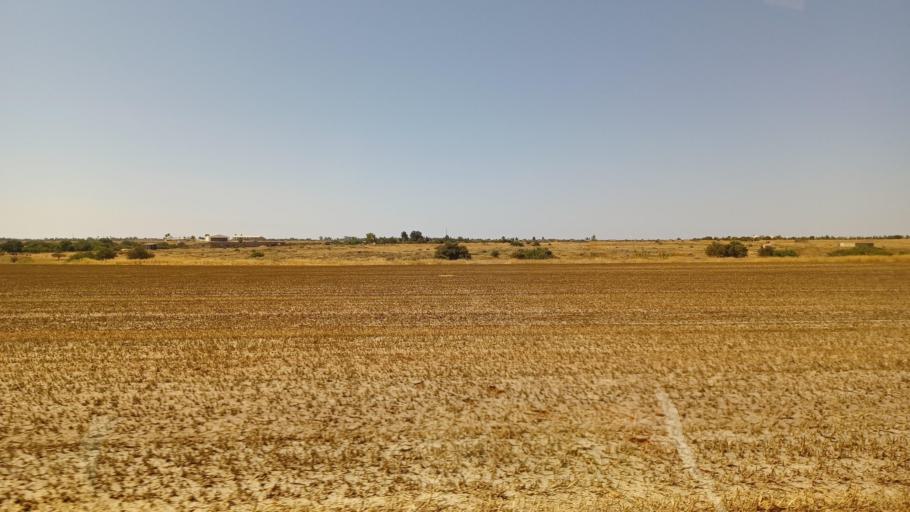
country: CY
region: Larnaka
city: Pergamos
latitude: 35.0249
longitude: 33.7194
